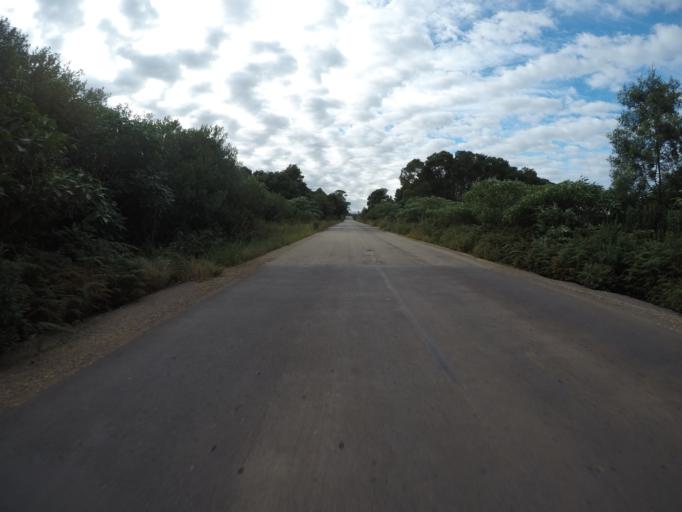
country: ZA
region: Eastern Cape
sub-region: Cacadu District Municipality
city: Kareedouw
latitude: -34.0055
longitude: 24.2380
